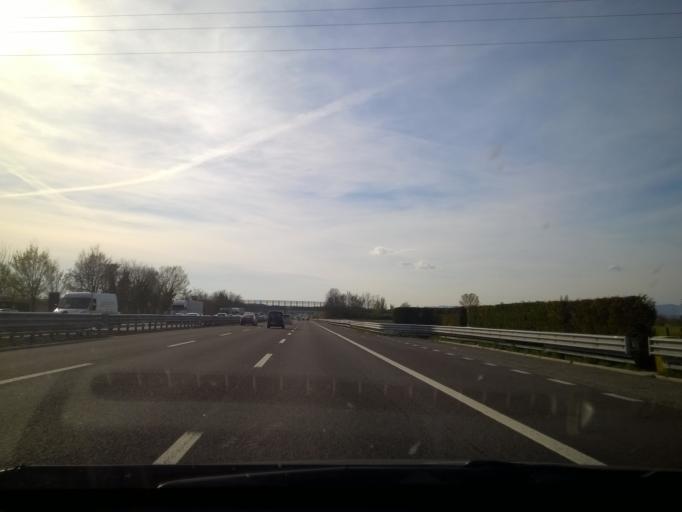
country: IT
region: Lombardy
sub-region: Provincia di Brescia
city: Desenzano del Garda
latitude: 45.4414
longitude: 10.5620
